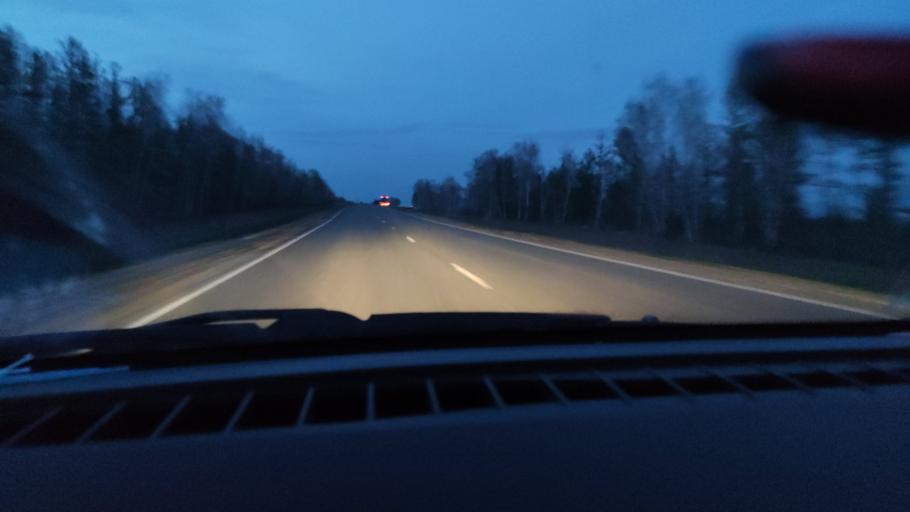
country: RU
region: Saratov
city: Sennoy
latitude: 52.1341
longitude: 46.8677
